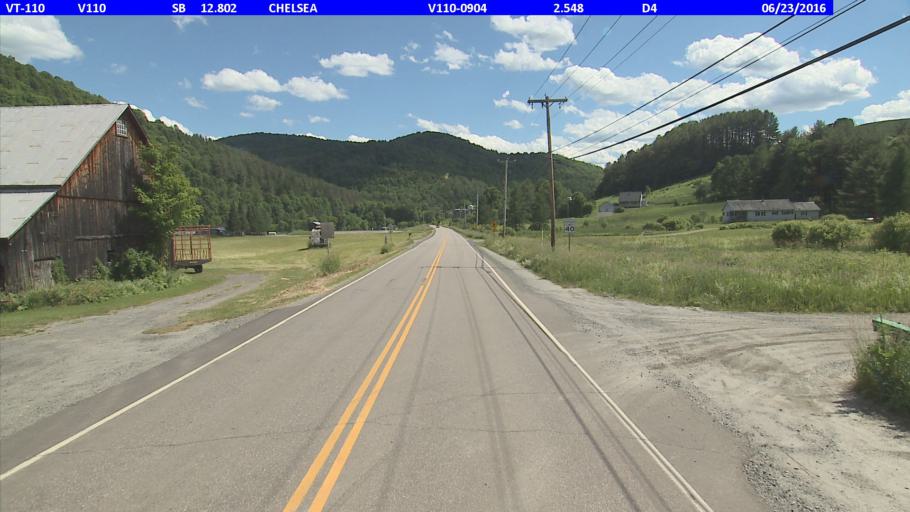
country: US
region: Vermont
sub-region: Orange County
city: Chelsea
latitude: 43.9831
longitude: -72.4483
